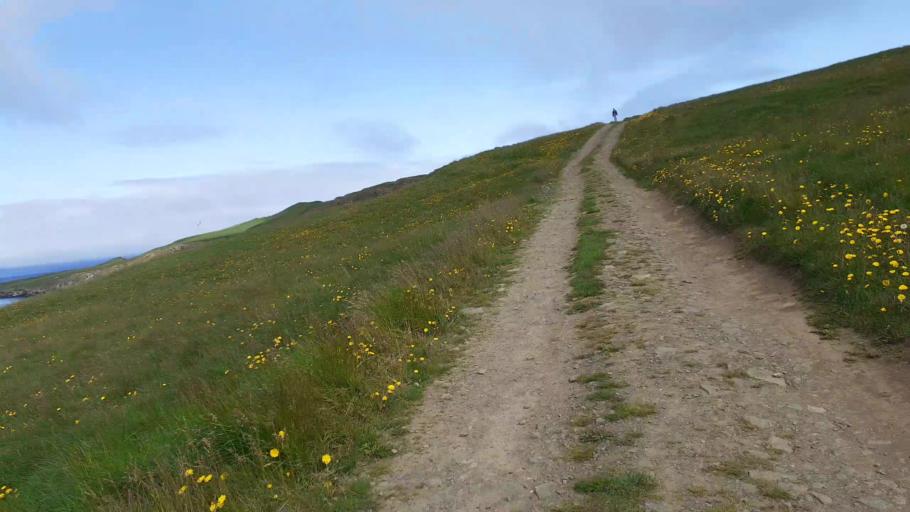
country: IS
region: Northeast
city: Dalvik
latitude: 66.5522
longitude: -18.0165
